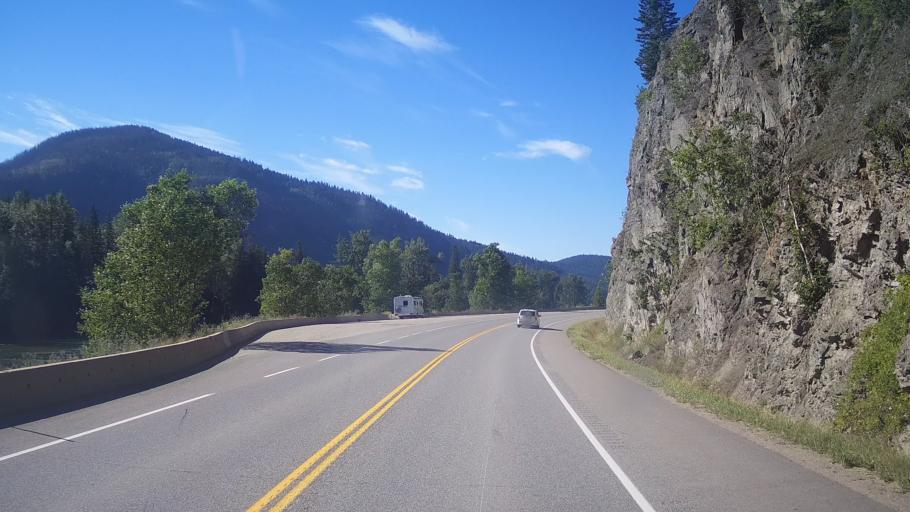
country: CA
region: British Columbia
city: Kamloops
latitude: 51.4638
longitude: -120.1771
